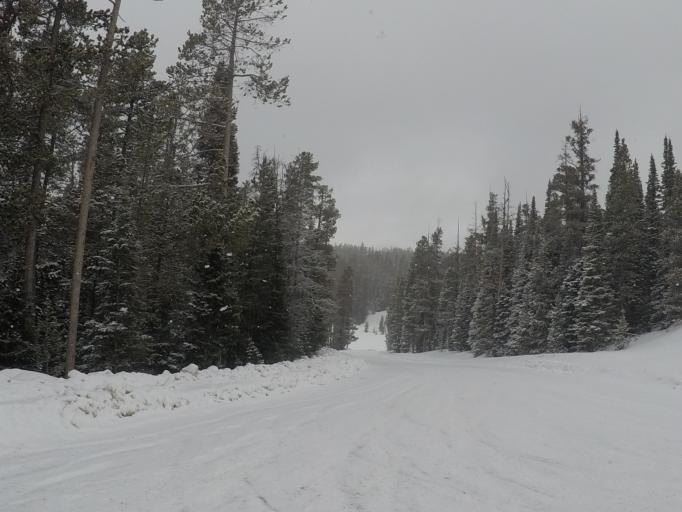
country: US
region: Montana
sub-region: Meagher County
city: White Sulphur Springs
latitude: 46.8376
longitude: -110.6962
